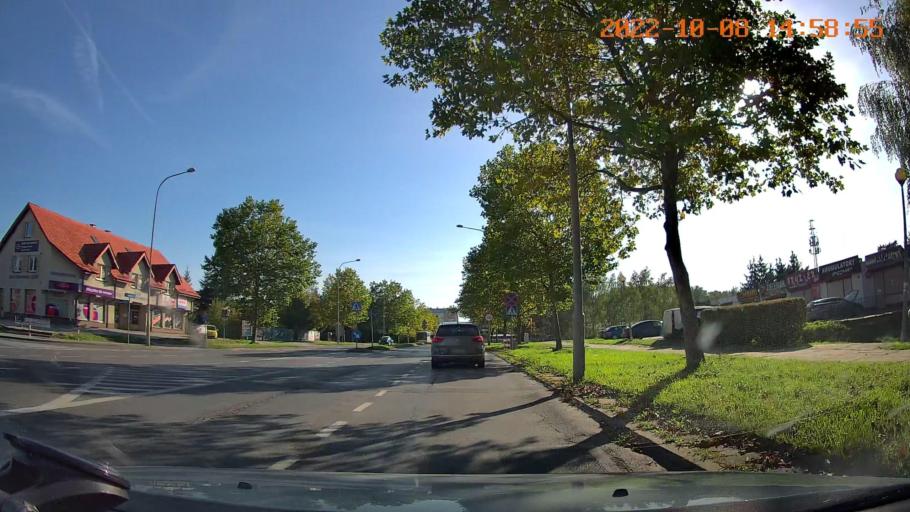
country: PL
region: Lesser Poland Voivodeship
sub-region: Powiat tarnowski
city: Tarnow
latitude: 50.0216
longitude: 20.9972
